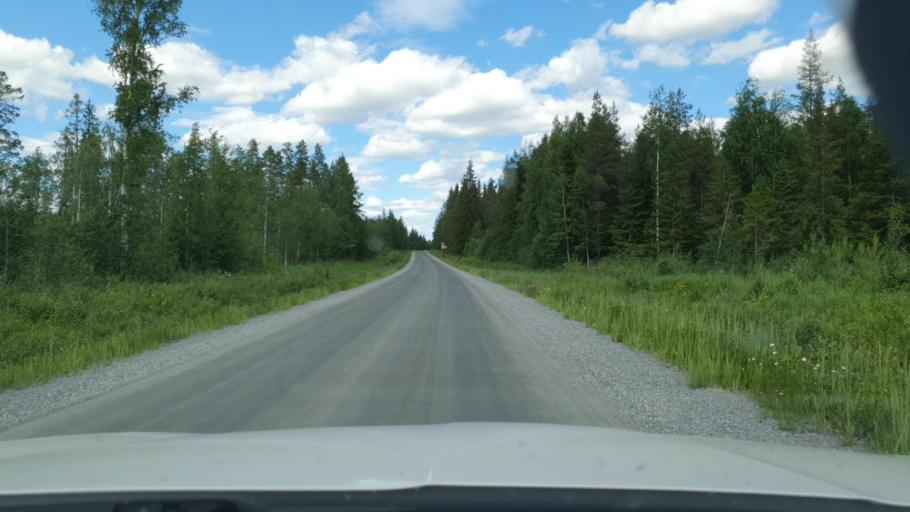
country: SE
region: Vaesterbotten
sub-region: Skelleftea Kommun
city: Forsbacka
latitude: 64.8217
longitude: 20.4962
